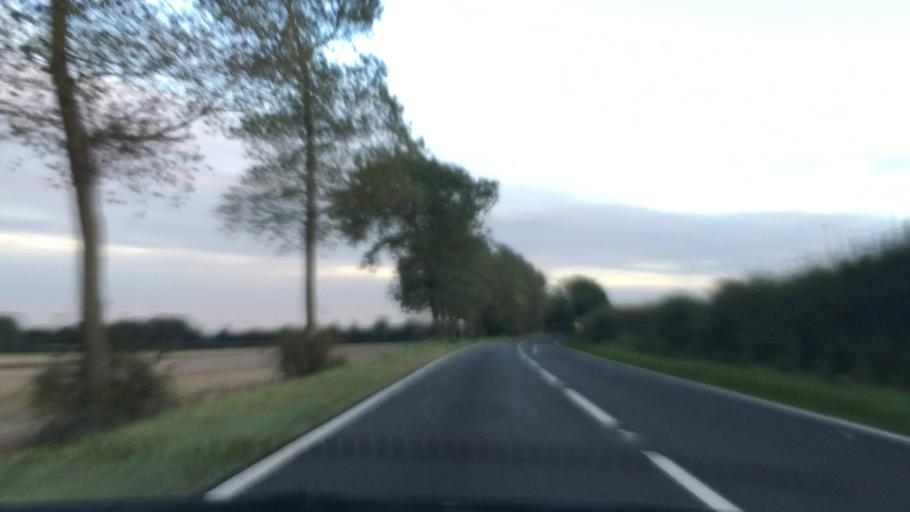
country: GB
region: England
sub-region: North East Lincolnshire
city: Wold Newton
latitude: 53.4716
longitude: -0.1099
